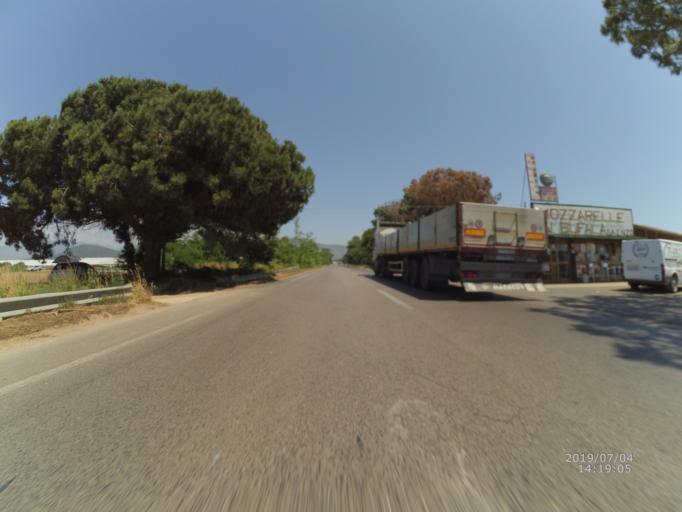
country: IT
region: Latium
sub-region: Provincia di Latina
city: Sperlonga
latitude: 41.2862
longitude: 13.3841
